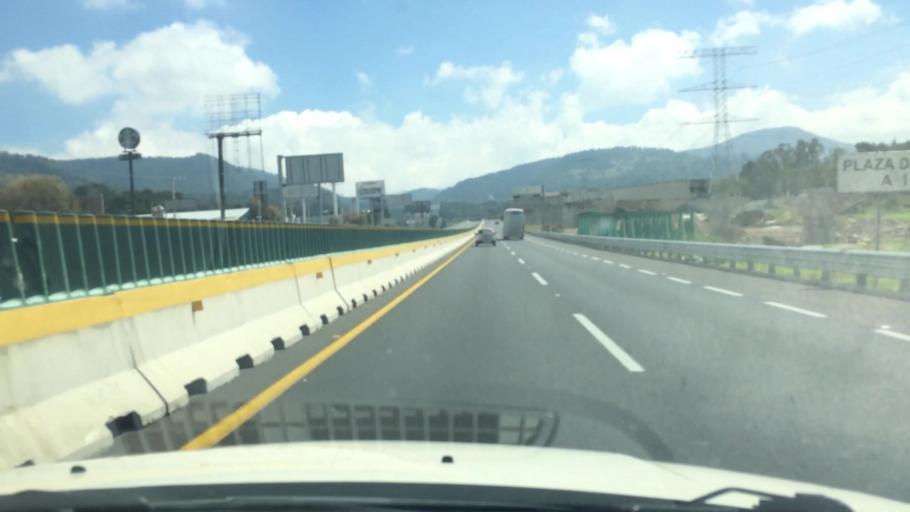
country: MX
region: Morelos
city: Ocoyoacac
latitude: 19.2870
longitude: -99.4470
